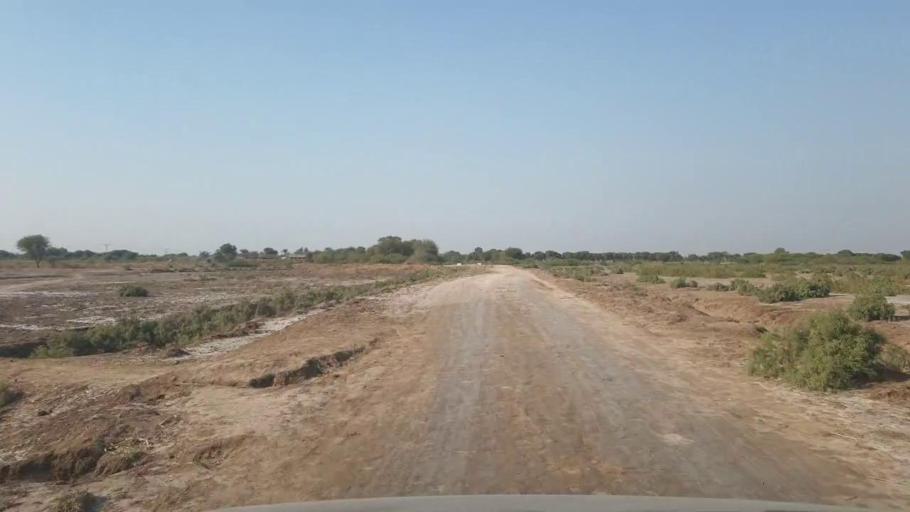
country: PK
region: Sindh
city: Chambar
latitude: 25.2999
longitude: 68.8628
